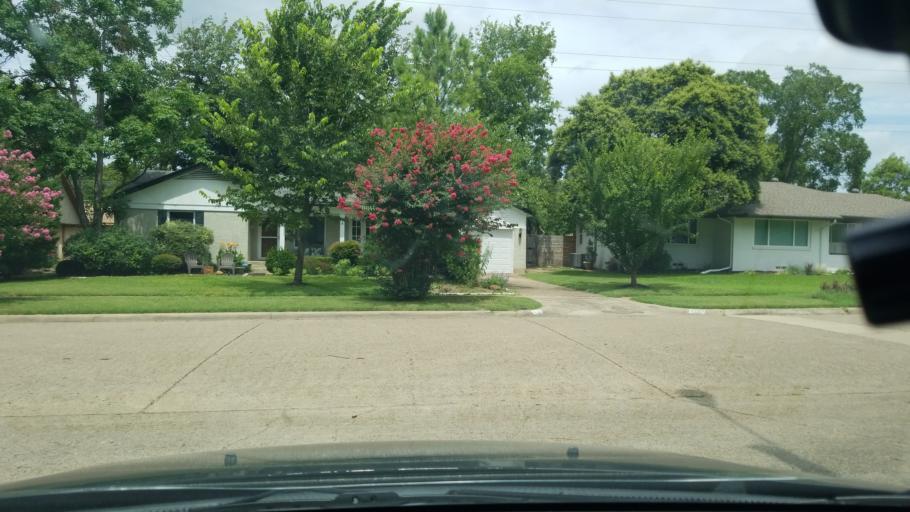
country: US
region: Texas
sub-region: Dallas County
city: Garland
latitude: 32.8291
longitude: -96.6919
